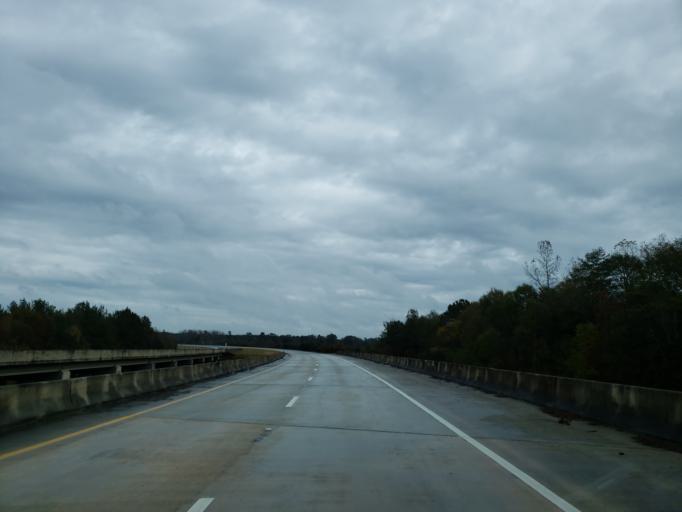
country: US
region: Mississippi
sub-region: Wayne County
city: Waynesboro
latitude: 31.6827
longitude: -88.6787
